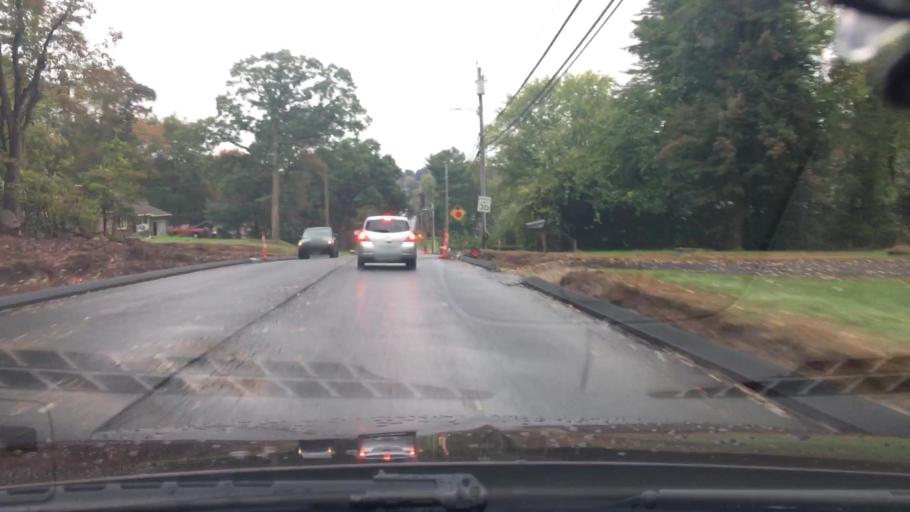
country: US
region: Connecticut
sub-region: Hartford County
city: Manchester
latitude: 41.8191
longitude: -72.5219
